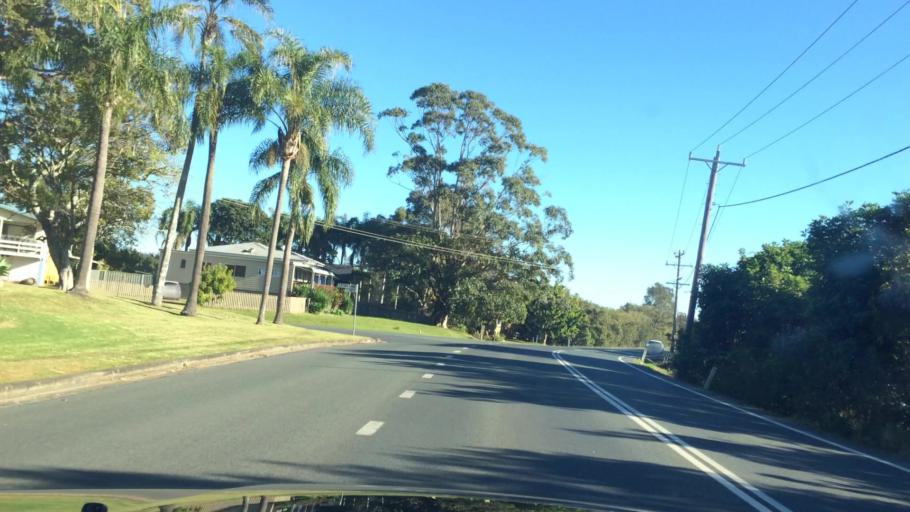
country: AU
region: New South Wales
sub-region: Port Macquarie-Hastings
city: North Shore
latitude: -31.4207
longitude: 152.8680
